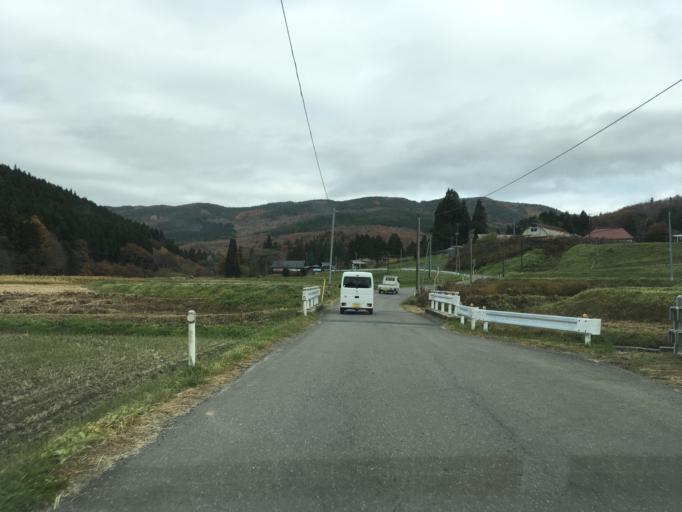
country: JP
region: Iwate
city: Mizusawa
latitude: 39.1079
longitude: 141.3278
